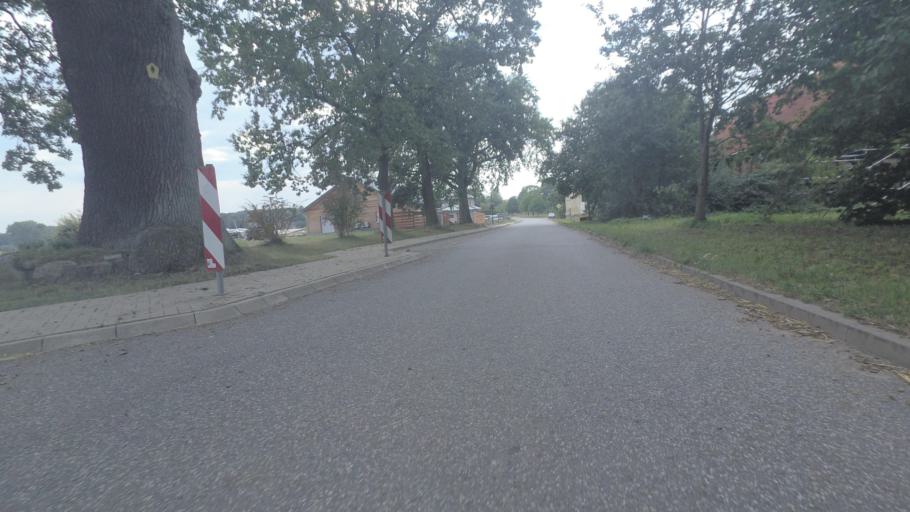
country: DE
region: Brandenburg
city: Heiligengrabe
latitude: 53.2433
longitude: 12.3624
